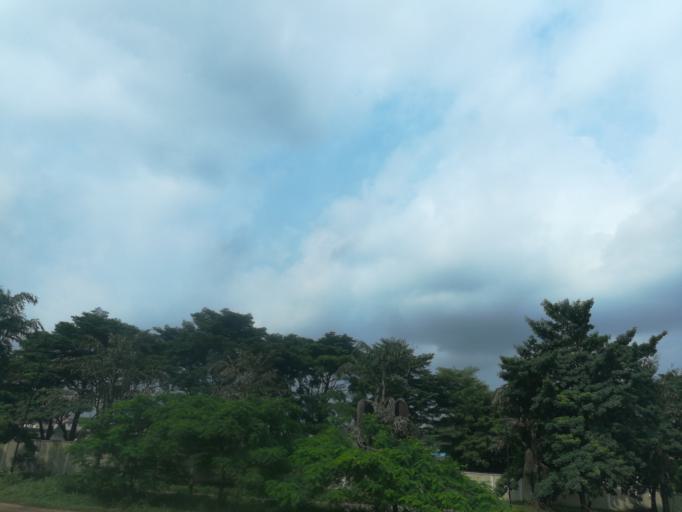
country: NG
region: Lagos
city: Ojota
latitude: 6.6123
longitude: 3.3686
